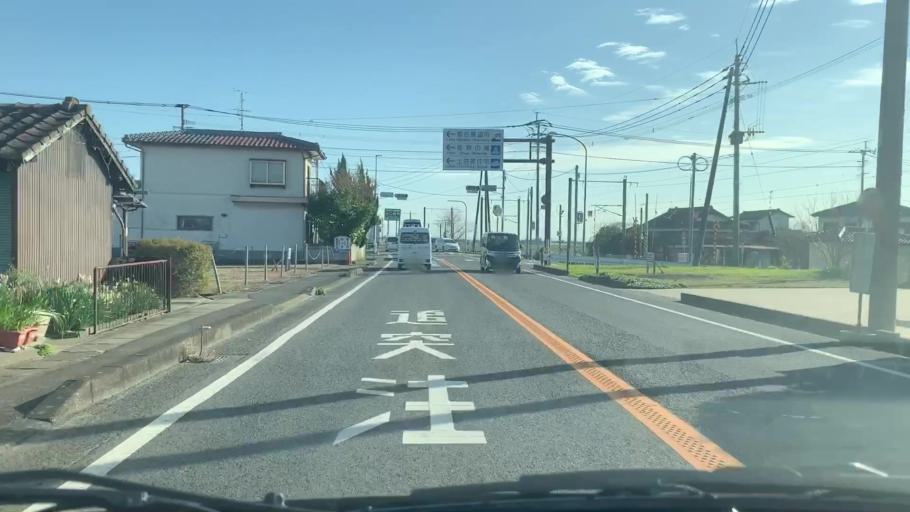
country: JP
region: Saga Prefecture
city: Takeocho-takeo
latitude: 33.2127
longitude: 130.1199
